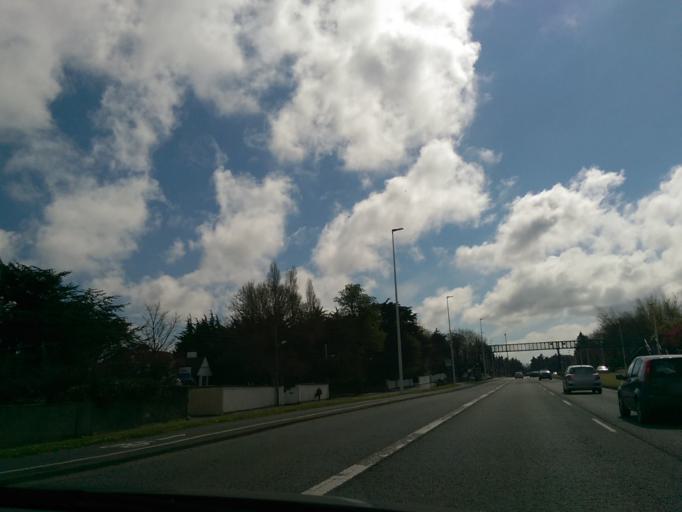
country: IE
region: Leinster
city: Mount Merrion
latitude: 53.3065
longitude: -6.2125
